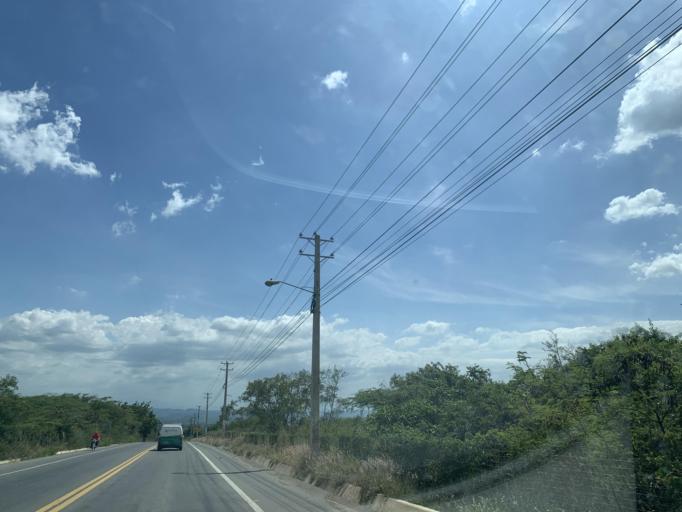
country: DO
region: Santiago
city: Villa Bisono
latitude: 19.5760
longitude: -70.8507
